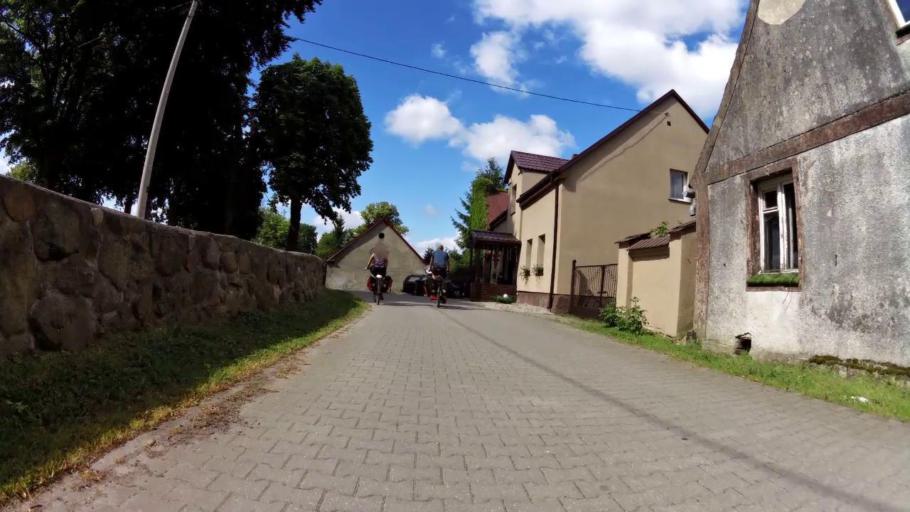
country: PL
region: West Pomeranian Voivodeship
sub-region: Powiat lobeski
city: Lobez
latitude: 53.6271
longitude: 15.6803
